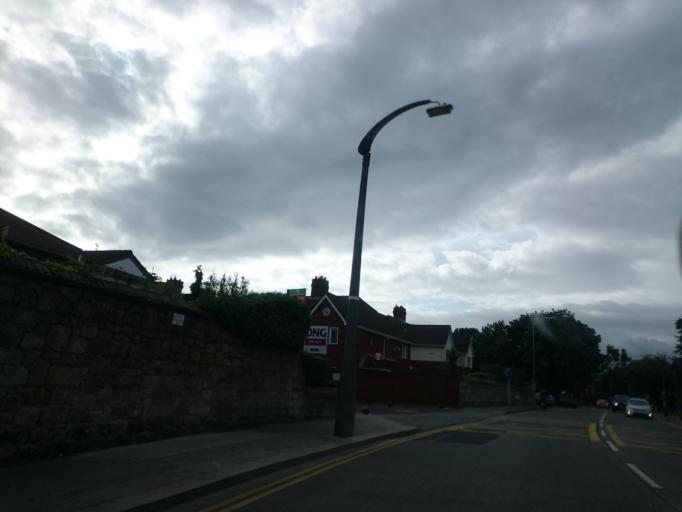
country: IE
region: Leinster
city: Rathgar
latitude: 53.3109
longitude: -6.2738
